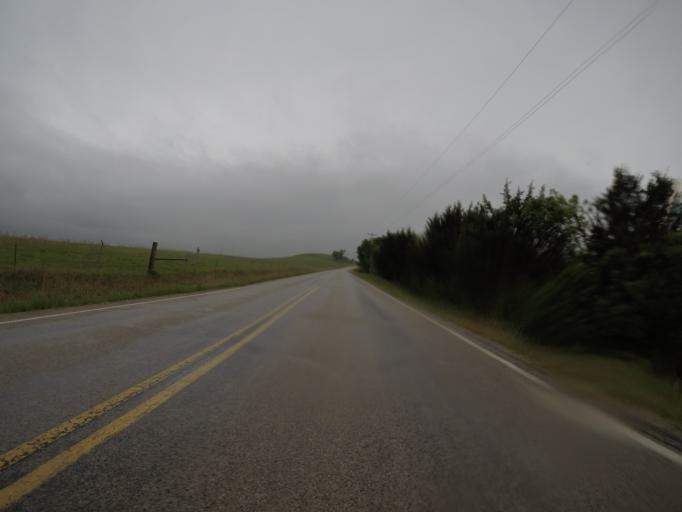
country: US
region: Kansas
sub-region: Pottawatomie County
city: Westmoreland
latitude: 39.4199
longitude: -96.1839
